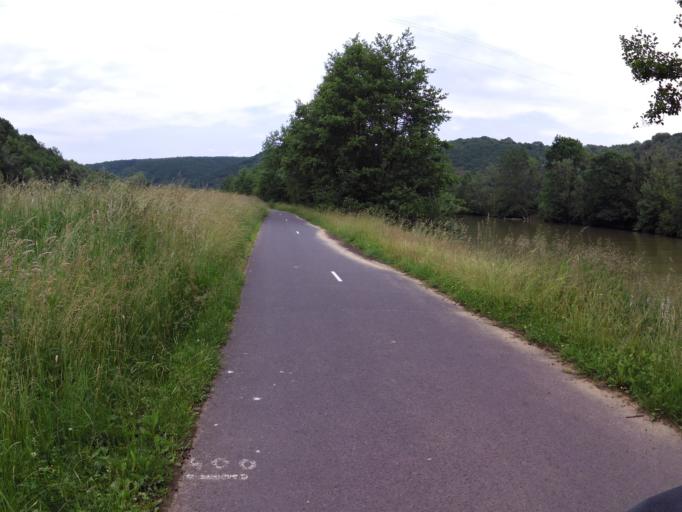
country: FR
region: Champagne-Ardenne
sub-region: Departement des Ardennes
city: Aiglemont
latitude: 49.7881
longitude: 4.7561
